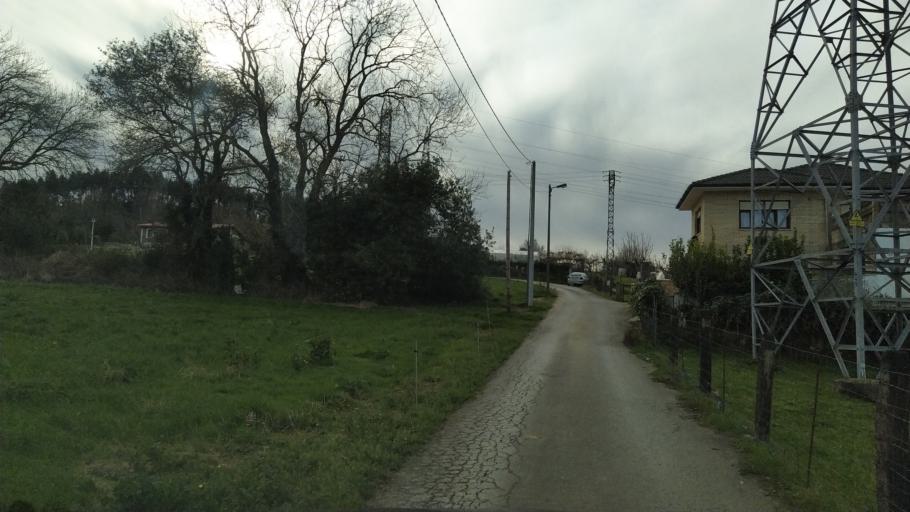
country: ES
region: Cantabria
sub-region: Provincia de Cantabria
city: Reocin
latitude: 43.3551
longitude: -4.0864
